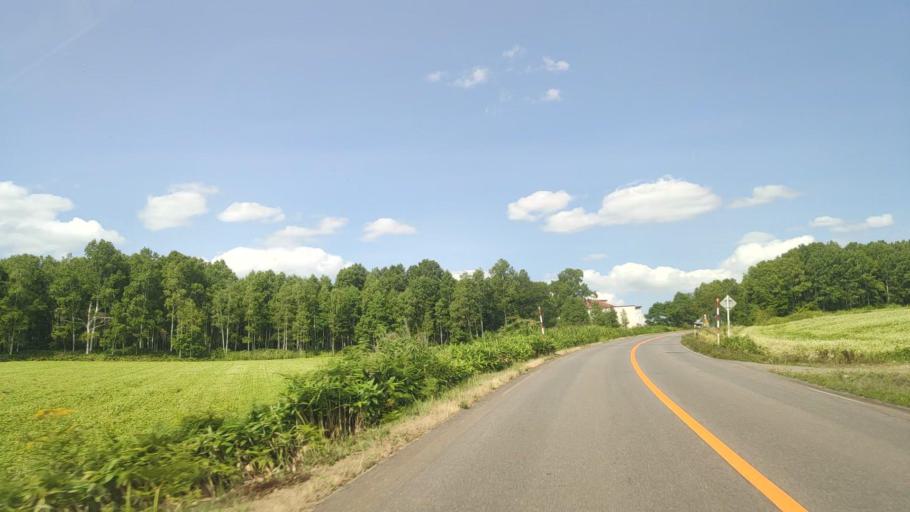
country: JP
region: Hokkaido
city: Nayoro
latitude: 44.2801
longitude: 142.4239
